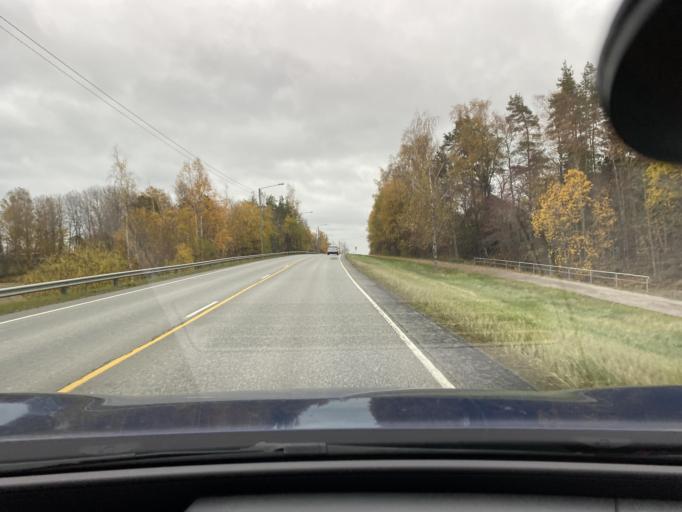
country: FI
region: Varsinais-Suomi
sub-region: Vakka-Suomi
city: Pyhaeranta
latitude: 60.9873
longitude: 21.5859
